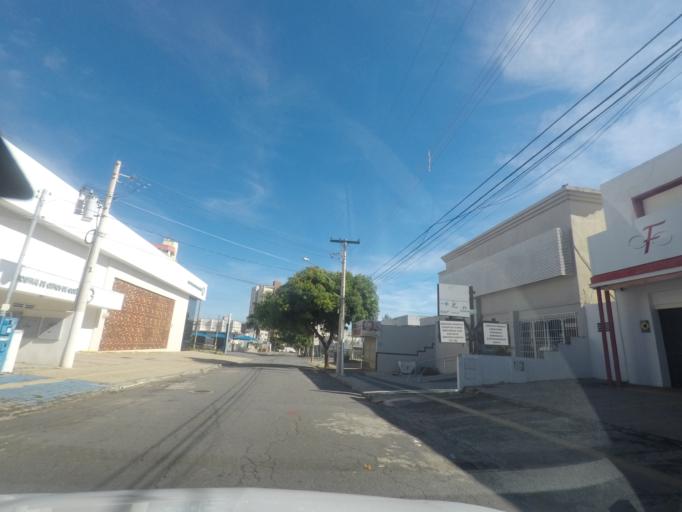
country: BR
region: Goias
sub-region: Goiania
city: Goiania
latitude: -16.6754
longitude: -49.2668
